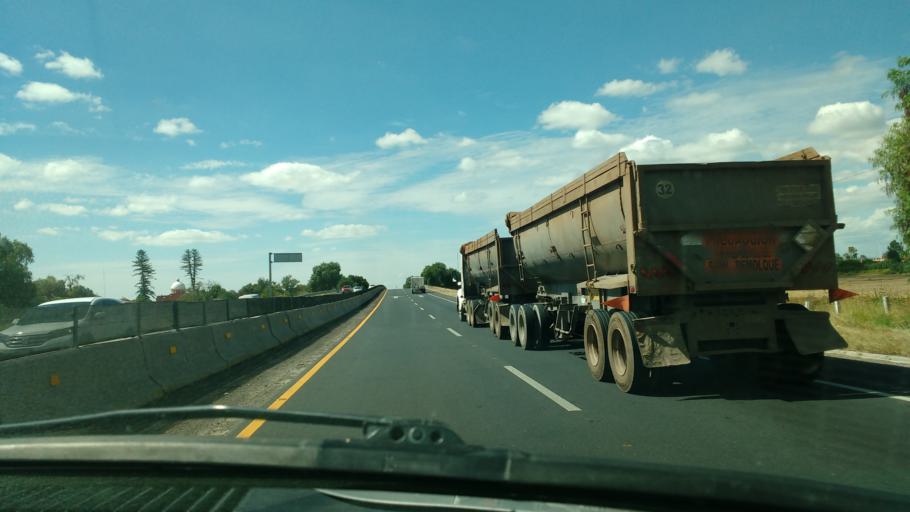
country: MX
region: Guanajuato
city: Apaseo el Grande
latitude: 20.5335
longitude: -100.6760
